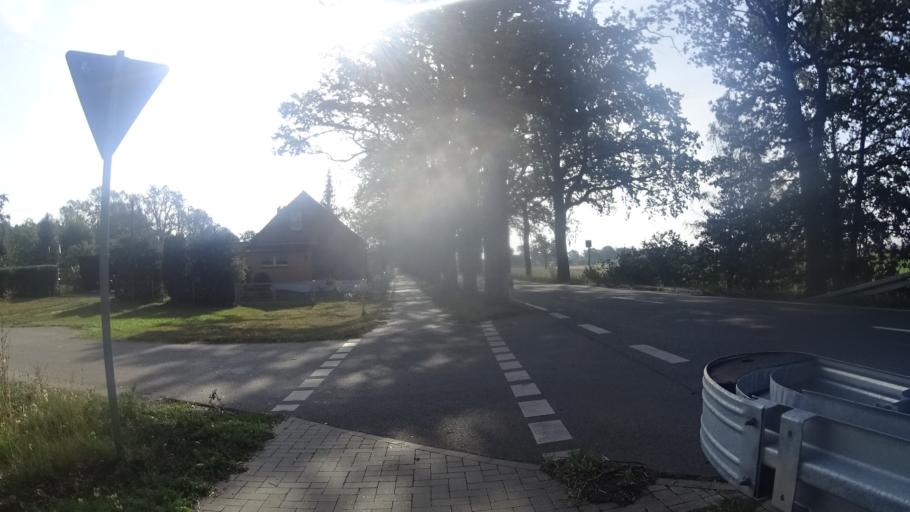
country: DE
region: Brandenburg
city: Cumlosen
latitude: 53.0280
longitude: 11.6626
